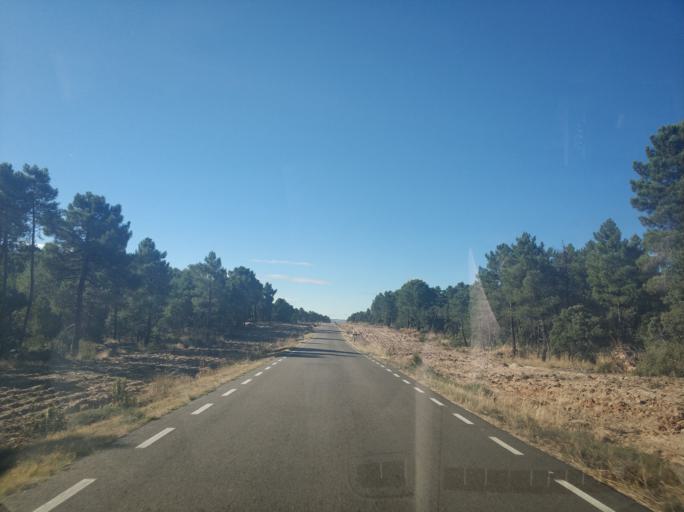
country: ES
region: Castille and Leon
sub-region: Provincia de Burgos
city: San Juan del Monte
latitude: 41.6675
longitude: -3.5285
